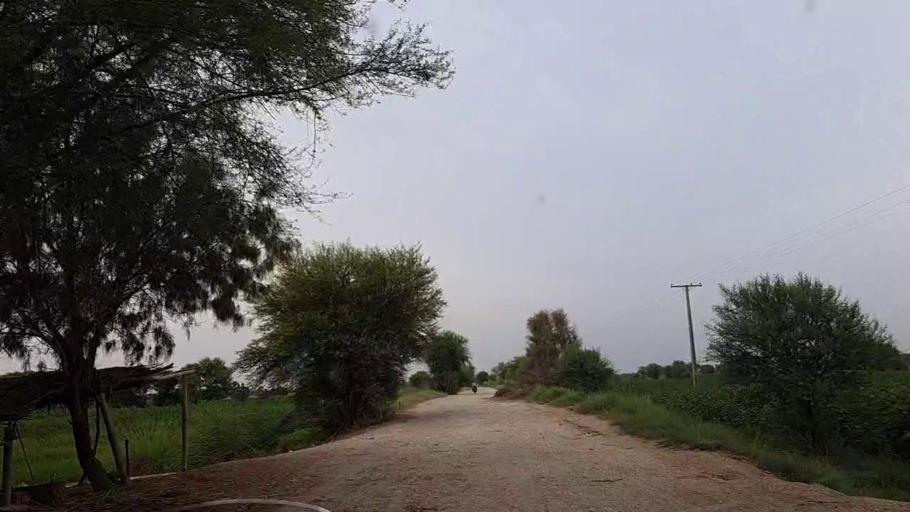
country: PK
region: Sindh
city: Mirpur Mathelo
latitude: 27.8534
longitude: 69.6310
